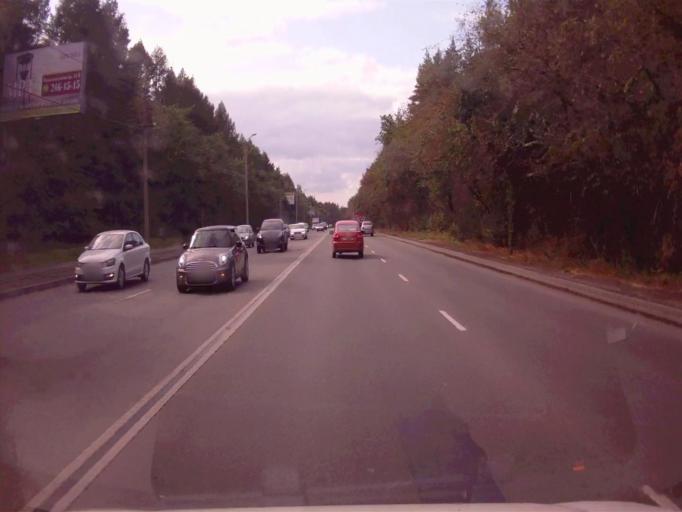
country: RU
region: Chelyabinsk
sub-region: Gorod Chelyabinsk
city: Chelyabinsk
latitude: 55.1469
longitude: 61.3410
